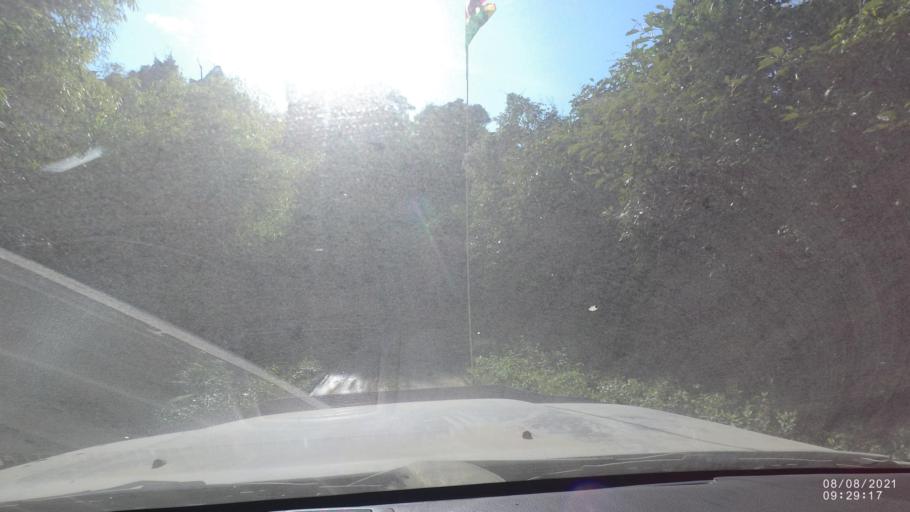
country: BO
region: La Paz
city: Quime
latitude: -16.5861
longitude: -66.7122
